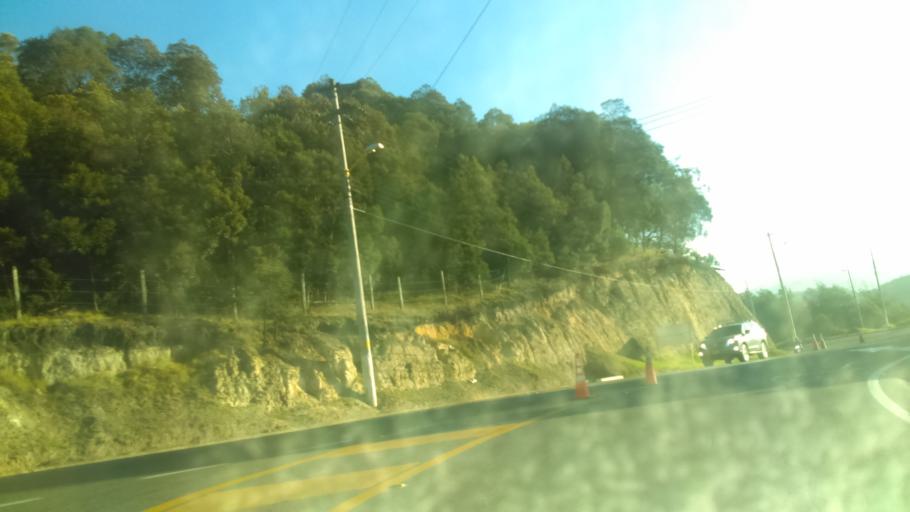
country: CO
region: Cundinamarca
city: San Antonio del Tequendama
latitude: 4.6350
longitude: -74.2954
